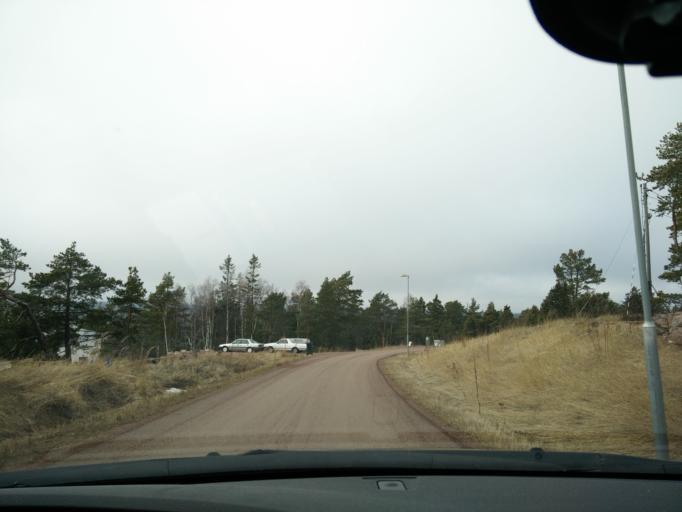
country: AX
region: Alands landsbygd
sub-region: Jomala
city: Jomala
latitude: 60.1307
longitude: 19.9276
